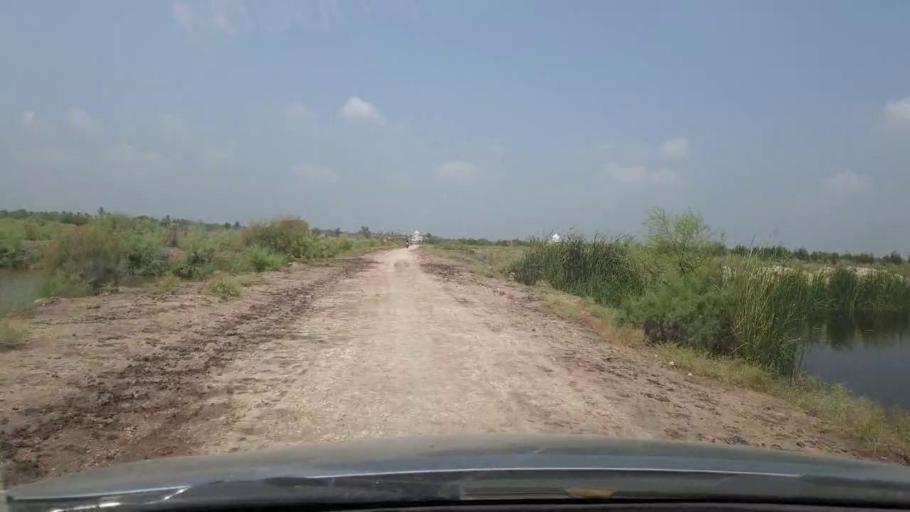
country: PK
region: Sindh
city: Khairpur
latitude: 27.4773
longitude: 68.6974
